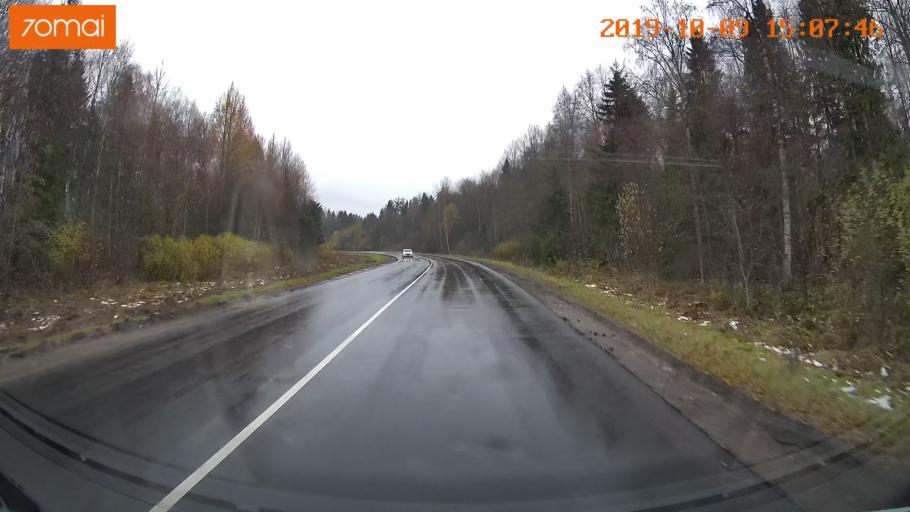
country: RU
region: Kostroma
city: Susanino
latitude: 58.2151
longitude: 41.6470
